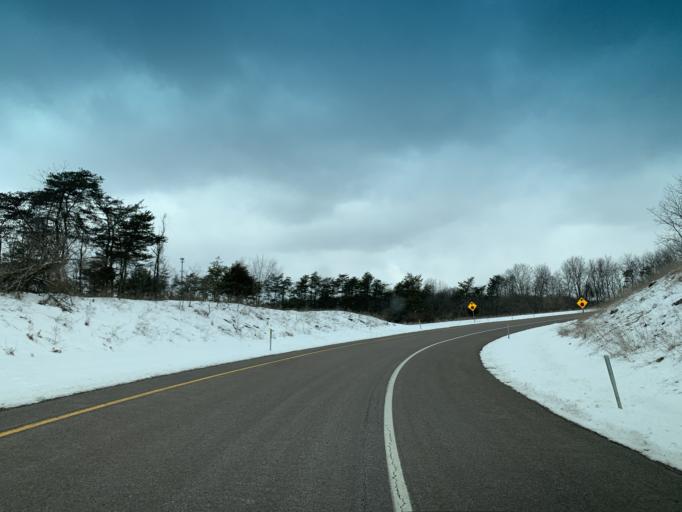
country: US
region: West Virginia
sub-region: Morgan County
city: Berkeley Springs
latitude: 39.6680
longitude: -78.4432
